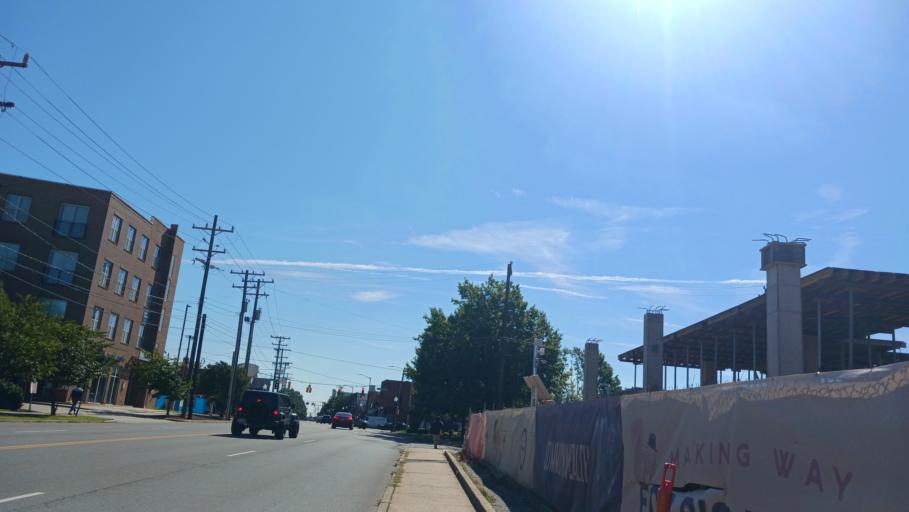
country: US
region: North Carolina
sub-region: Mecklenburg County
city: Charlotte
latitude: 35.2205
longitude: -80.8147
